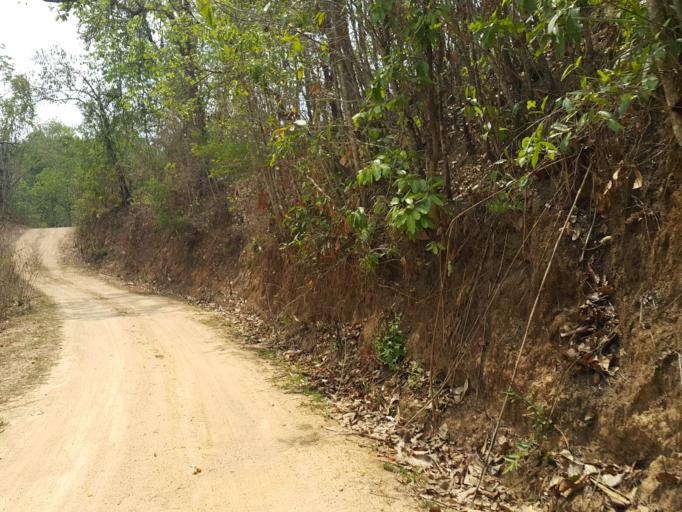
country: TH
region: Chiang Mai
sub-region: Amphoe Chiang Dao
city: Chiang Dao
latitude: 19.3076
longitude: 98.7330
